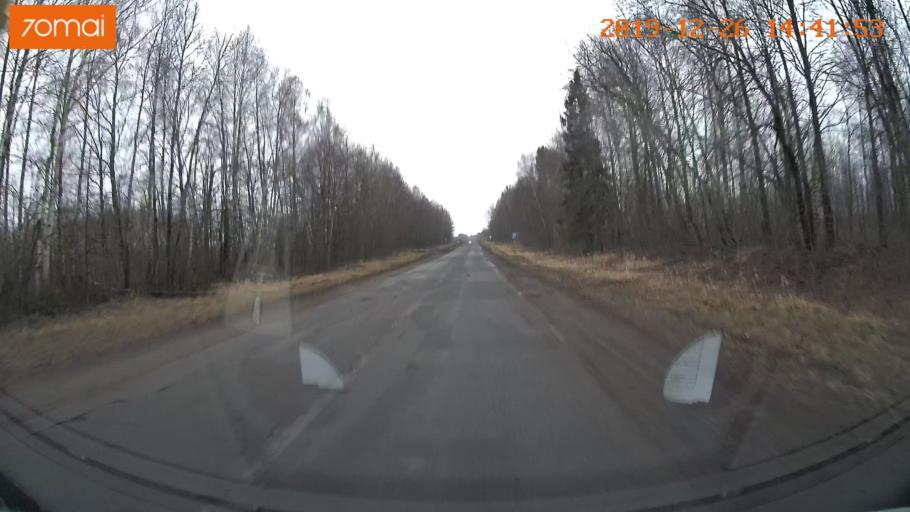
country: RU
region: Jaroslavl
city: Poshekhon'ye
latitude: 58.3678
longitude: 39.0244
